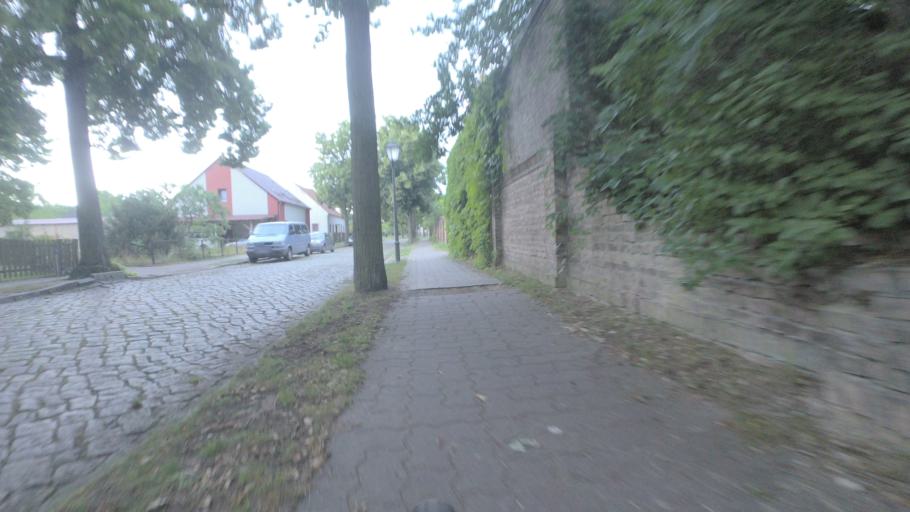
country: DE
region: Brandenburg
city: Bestensee
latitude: 52.2263
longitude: 13.6565
